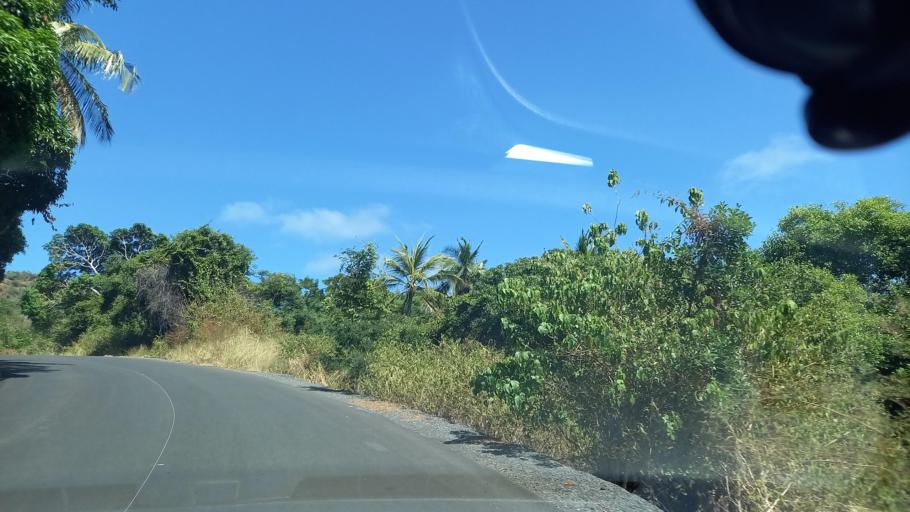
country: YT
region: Kani-Keli
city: Kani Keli
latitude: -12.9682
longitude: 45.1112
